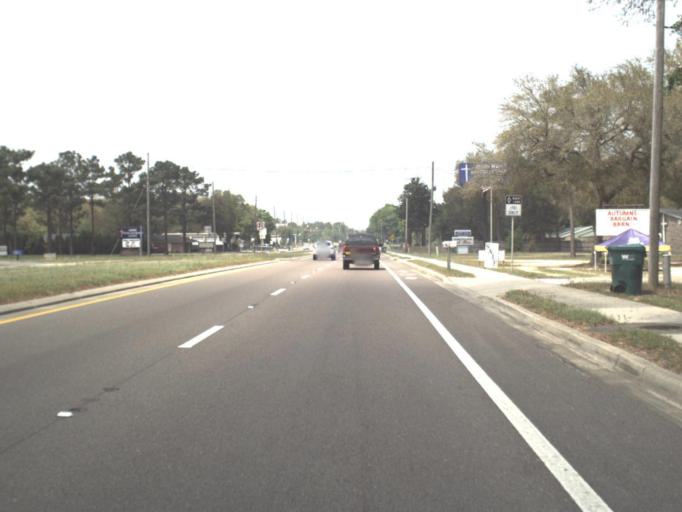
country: US
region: Florida
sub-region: Santa Rosa County
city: Milton
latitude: 30.6511
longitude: -87.0552
